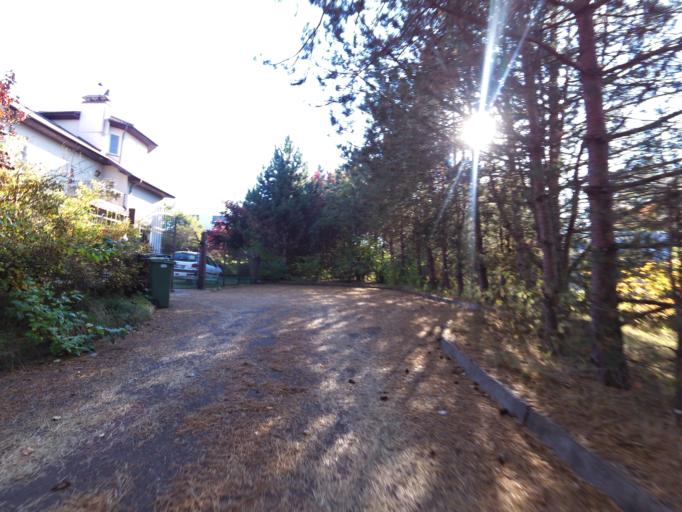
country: LT
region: Vilnius County
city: Pasilaiciai
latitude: 54.7338
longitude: 25.1929
